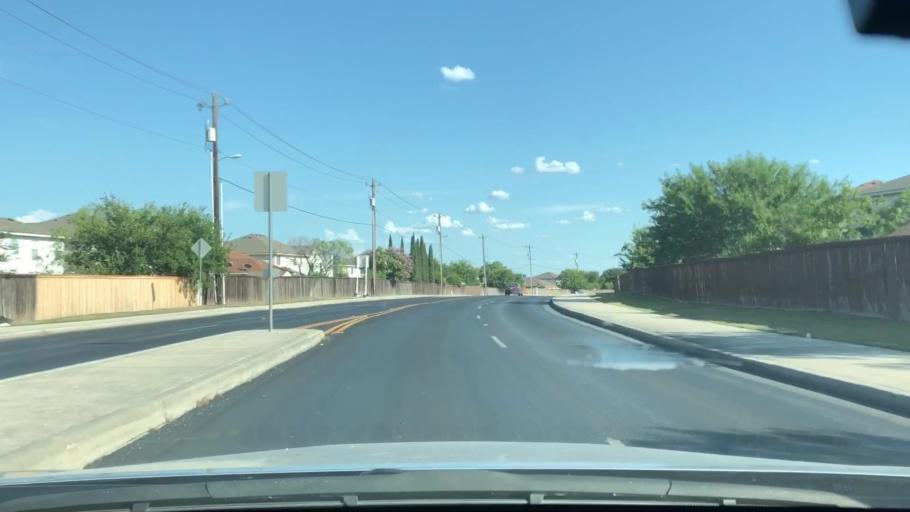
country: US
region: Texas
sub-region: Bexar County
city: Kirby
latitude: 29.4767
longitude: -98.3466
